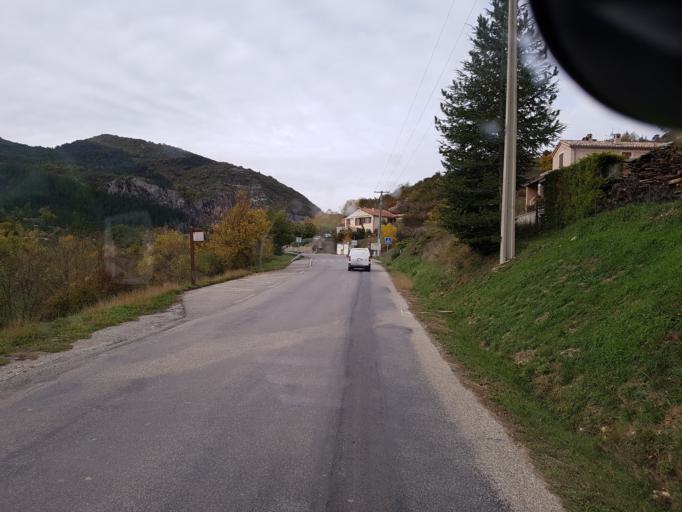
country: FR
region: Provence-Alpes-Cote d'Azur
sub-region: Departement des Hautes-Alpes
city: Laragne-Monteglin
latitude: 44.3143
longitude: 5.7030
